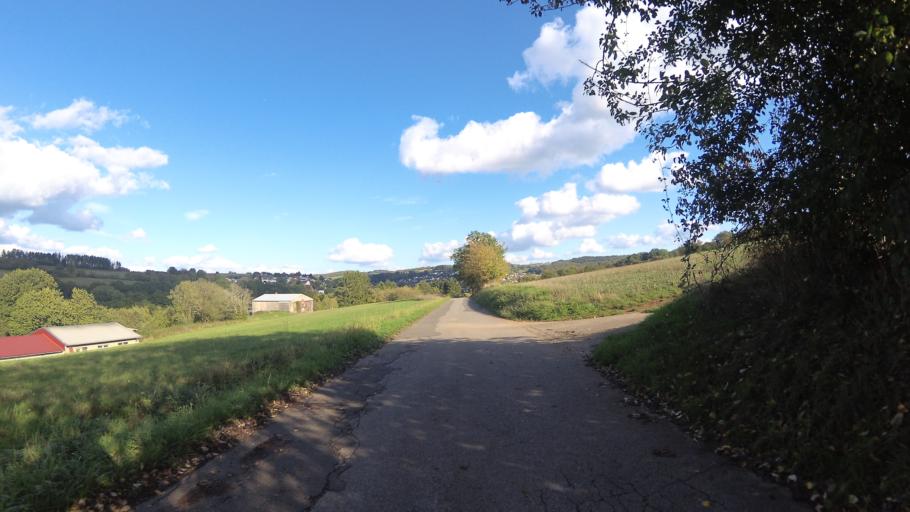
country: DE
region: Saarland
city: Marpingen
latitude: 49.4549
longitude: 7.0423
